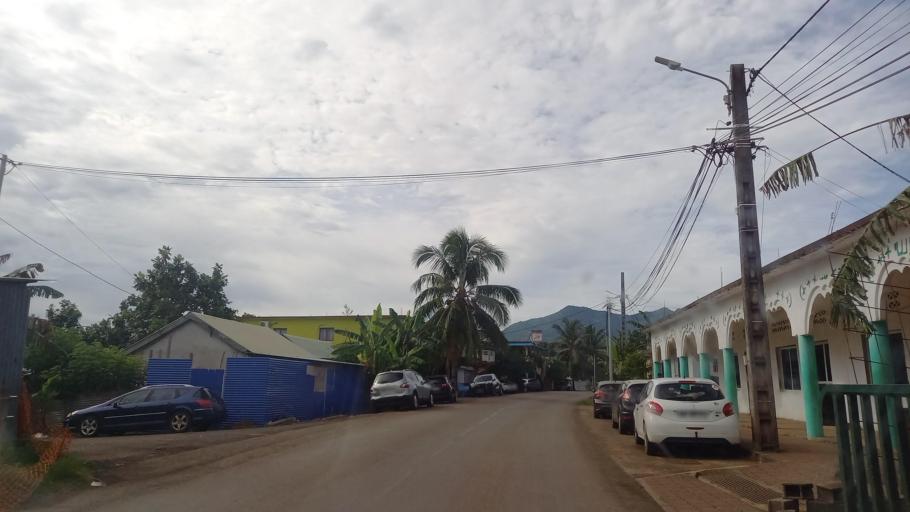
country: YT
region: Chirongui
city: Chirongui
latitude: -12.9295
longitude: 45.1530
